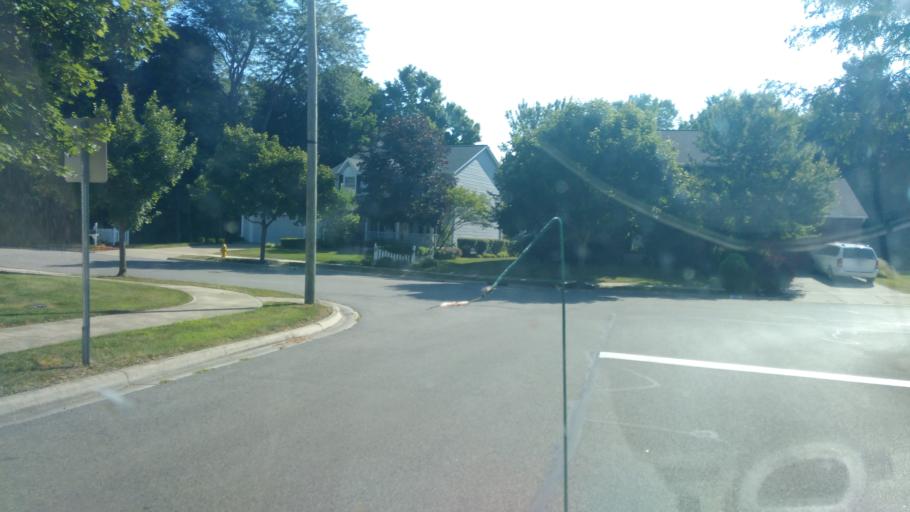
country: US
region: Ohio
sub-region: Delaware County
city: Delaware
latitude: 40.3246
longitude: -83.0778
